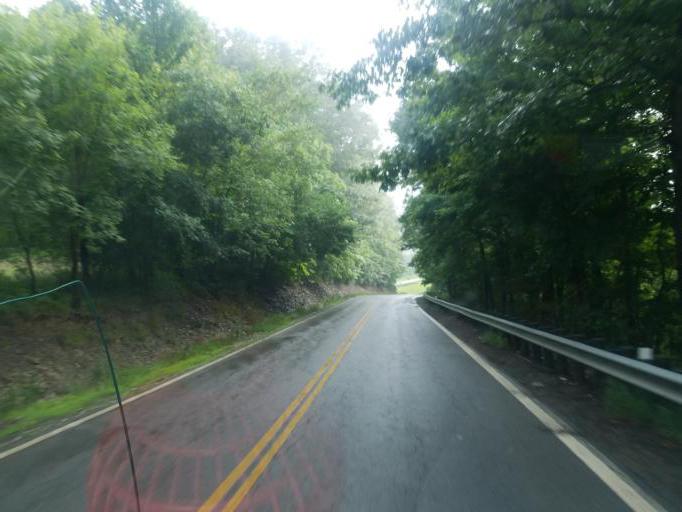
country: US
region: Ohio
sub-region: Medina County
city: Lodi
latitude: 40.9410
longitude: -82.0108
